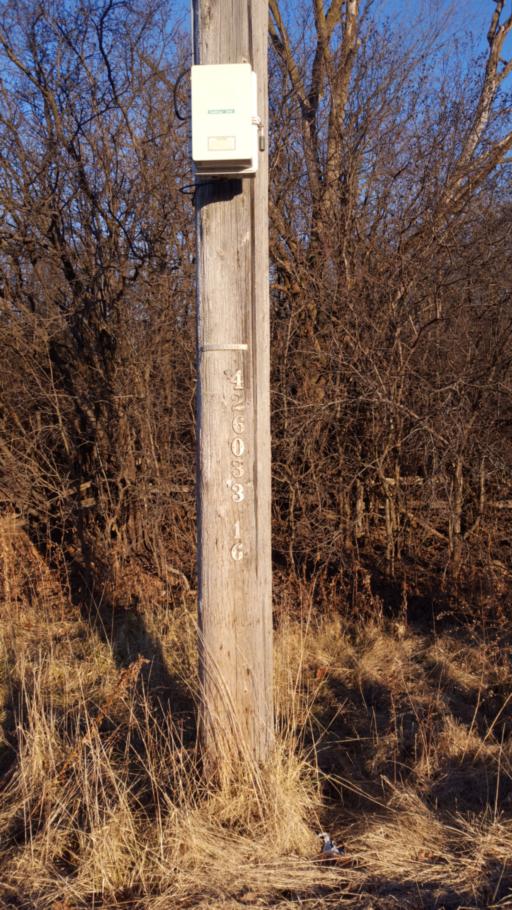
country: US
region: Illinois
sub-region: Cook County
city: Northbrook
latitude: 42.1416
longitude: -87.8279
